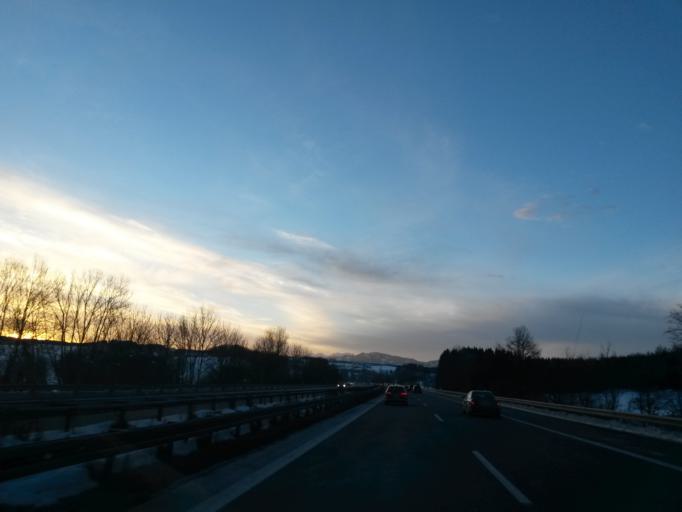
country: DE
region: Bavaria
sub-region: Swabia
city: Betzigau
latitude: 47.7296
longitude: 10.3509
